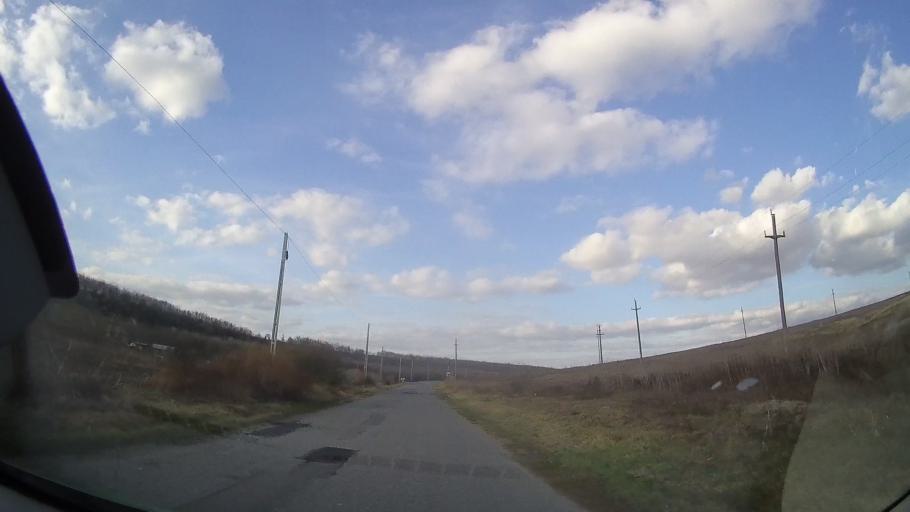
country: RO
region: Constanta
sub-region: Comuna Cerchezu
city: Cerchezu
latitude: 43.8286
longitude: 28.0972
